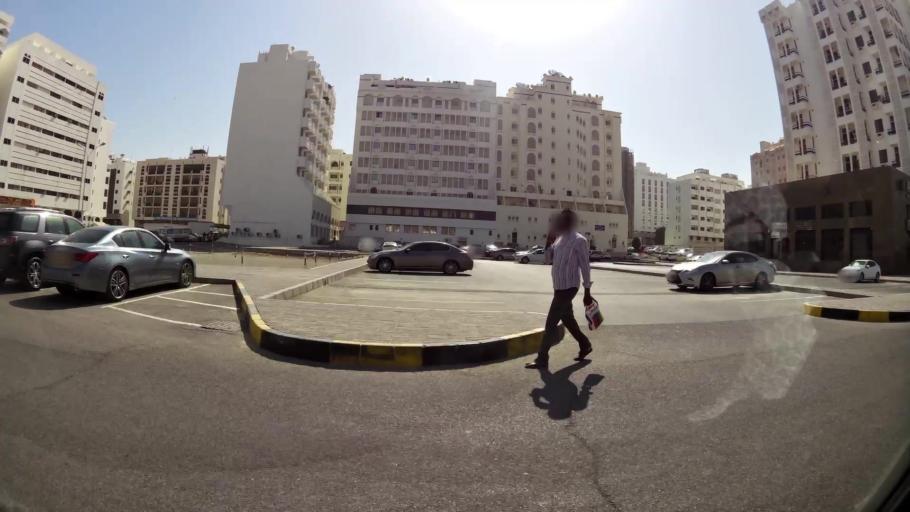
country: OM
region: Muhafazat Masqat
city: Muscat
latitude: 23.5981
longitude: 58.5470
